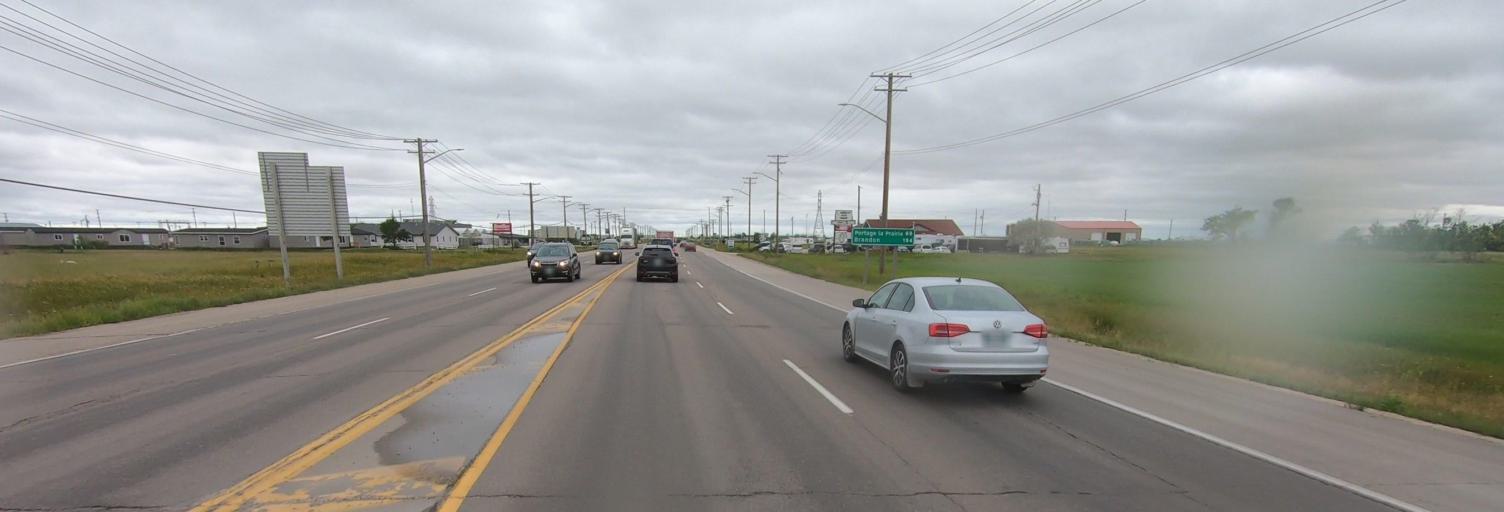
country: CA
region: Manitoba
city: Headingley
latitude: 49.8786
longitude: -97.3421
